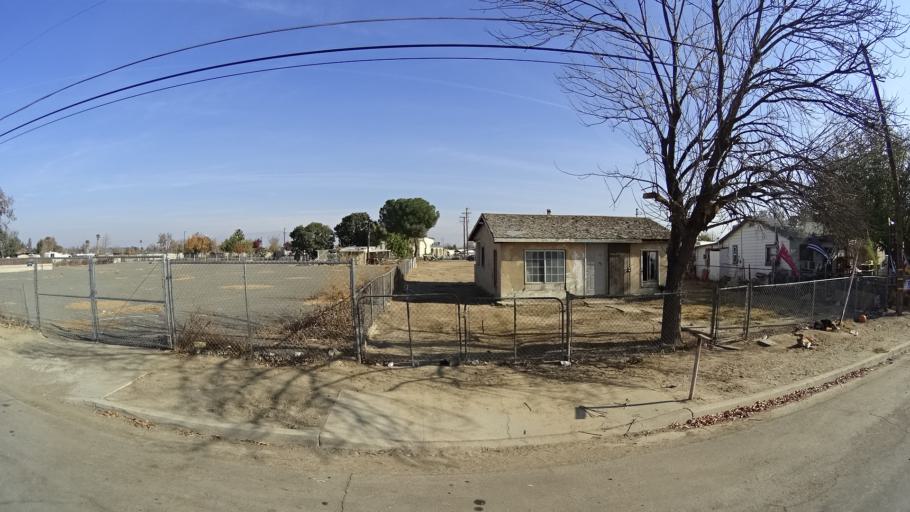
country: US
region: California
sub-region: Kern County
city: Bakersfield
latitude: 35.3331
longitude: -119.0130
